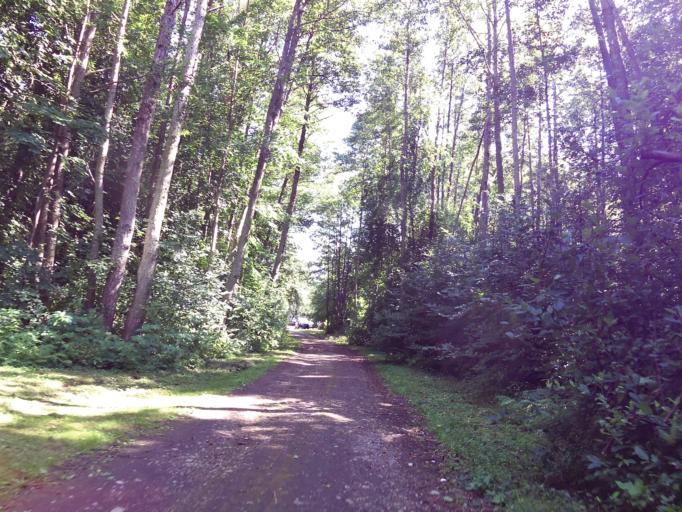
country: EE
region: Hiiumaa
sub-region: Kaerdla linn
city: Kardla
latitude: 58.9331
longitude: 22.3898
